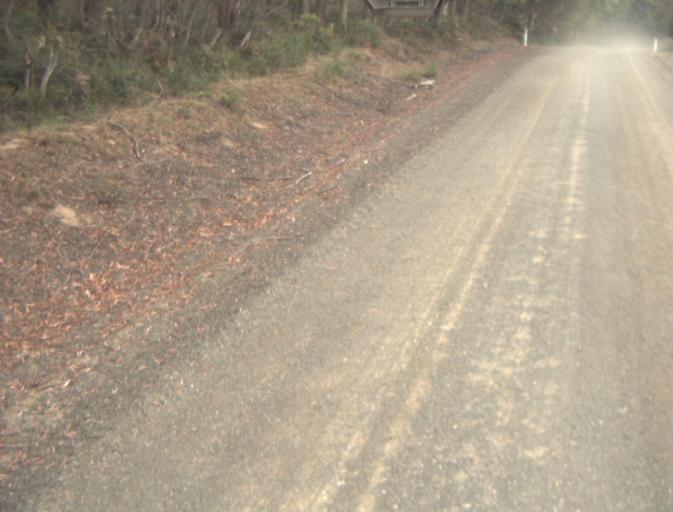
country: AU
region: Tasmania
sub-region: Dorset
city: Scottsdale
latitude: -41.4547
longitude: 147.5294
